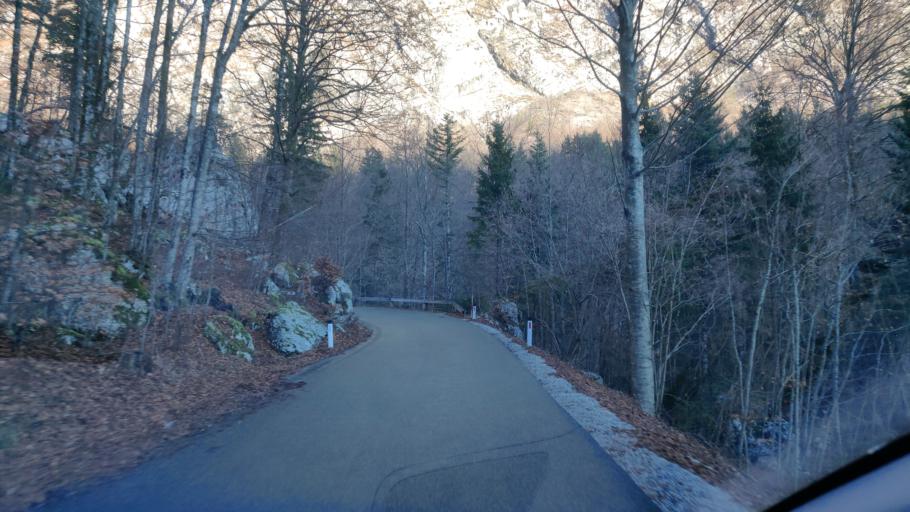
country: SI
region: Tolmin
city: Tolmin
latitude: 46.2887
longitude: 13.8069
